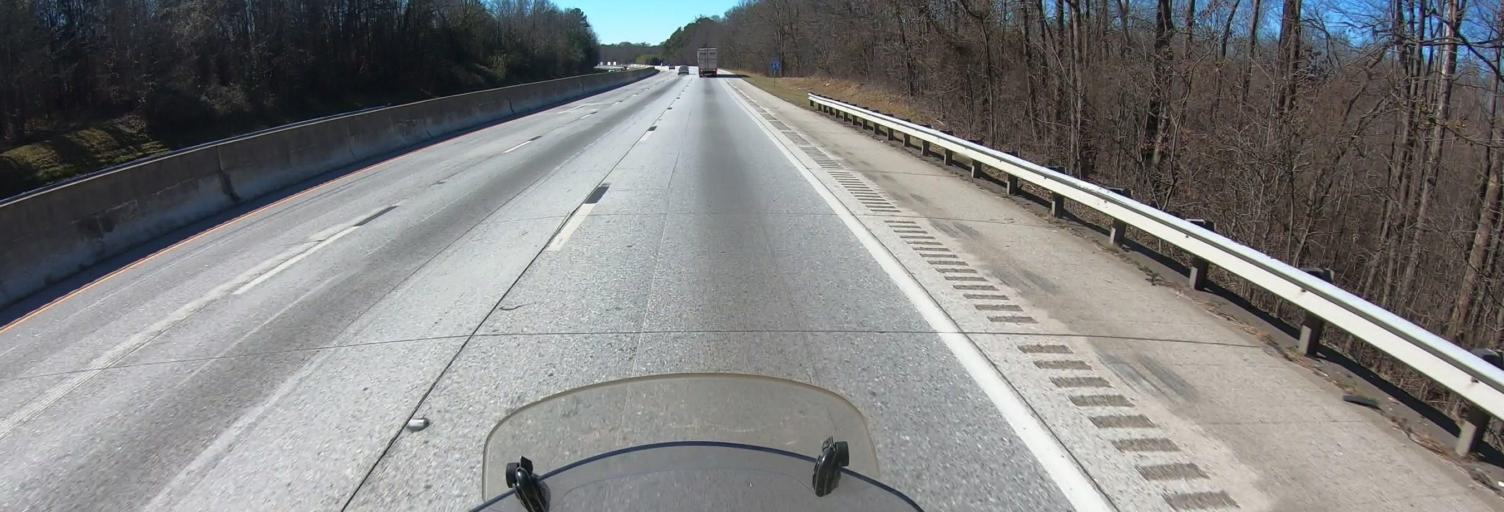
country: US
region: South Carolina
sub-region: Anderson County
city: Piedmont
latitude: 34.6721
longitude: -82.5438
